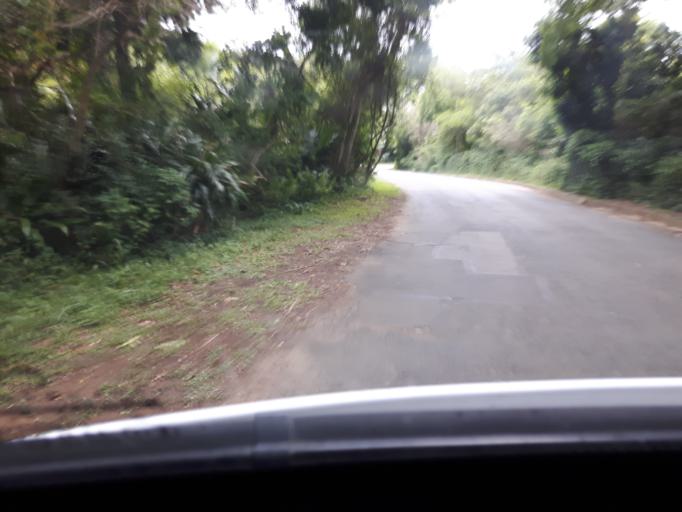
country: ZA
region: KwaZulu-Natal
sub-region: uMkhanyakude District Municipality
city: Mtubatuba
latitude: -28.3826
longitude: 32.4112
